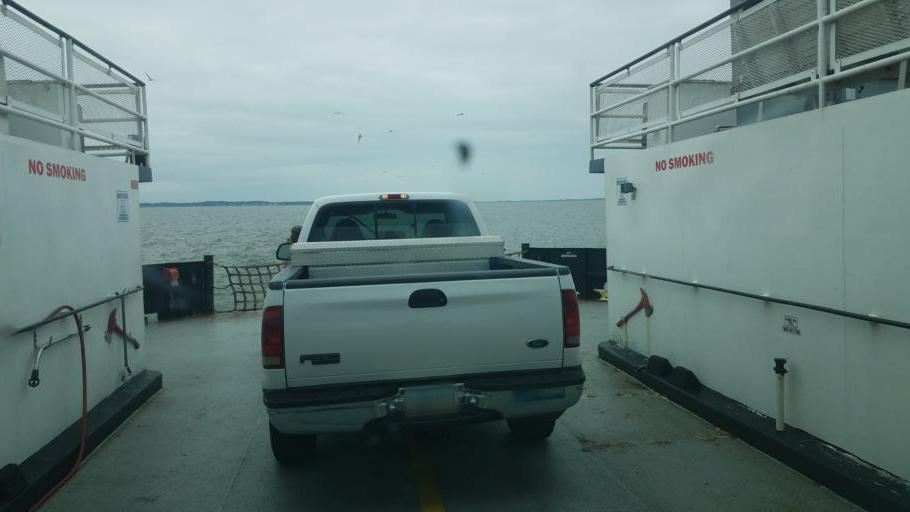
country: US
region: North Carolina
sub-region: Currituck County
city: Currituck
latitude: 36.4611
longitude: -75.9731
